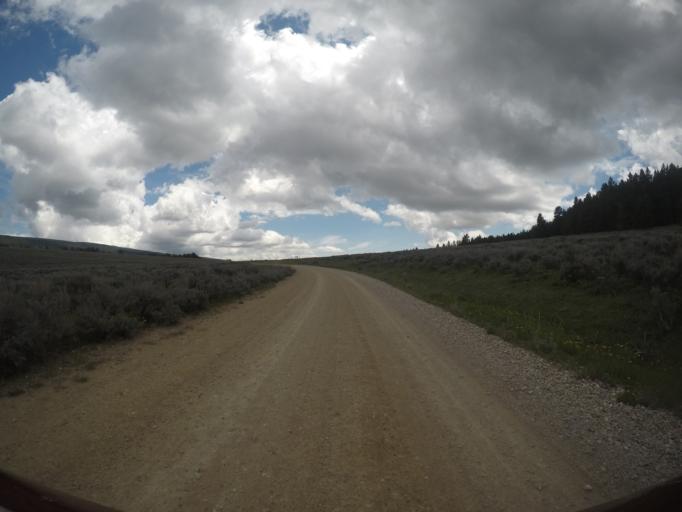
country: US
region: Wyoming
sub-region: Big Horn County
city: Lovell
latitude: 45.1721
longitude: -108.4548
